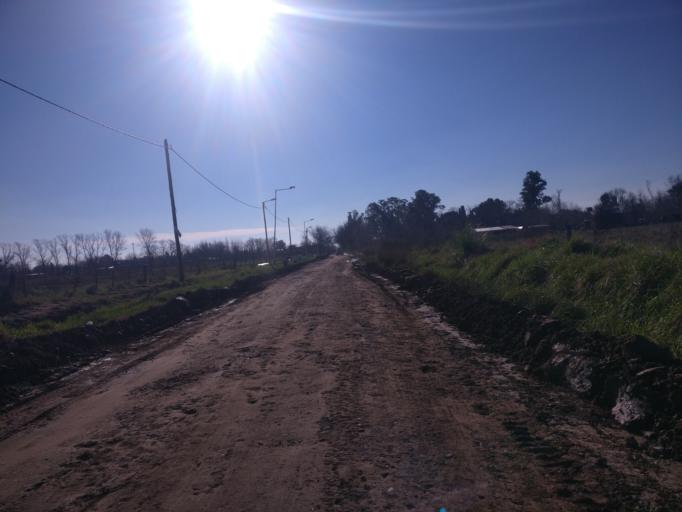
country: AR
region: Buenos Aires
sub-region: Partido de Ezeiza
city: Ezeiza
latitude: -34.9373
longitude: -58.6111
